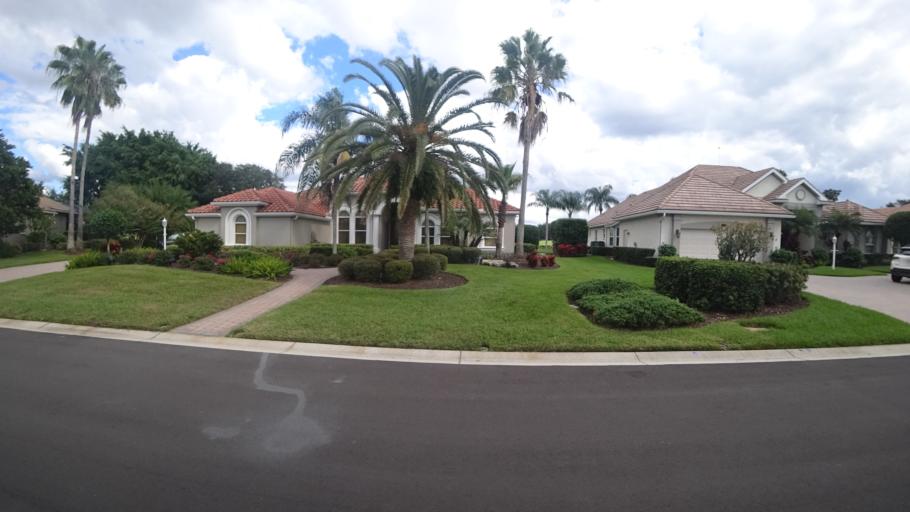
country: US
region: Florida
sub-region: Sarasota County
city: The Meadows
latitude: 27.3965
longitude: -82.4169
